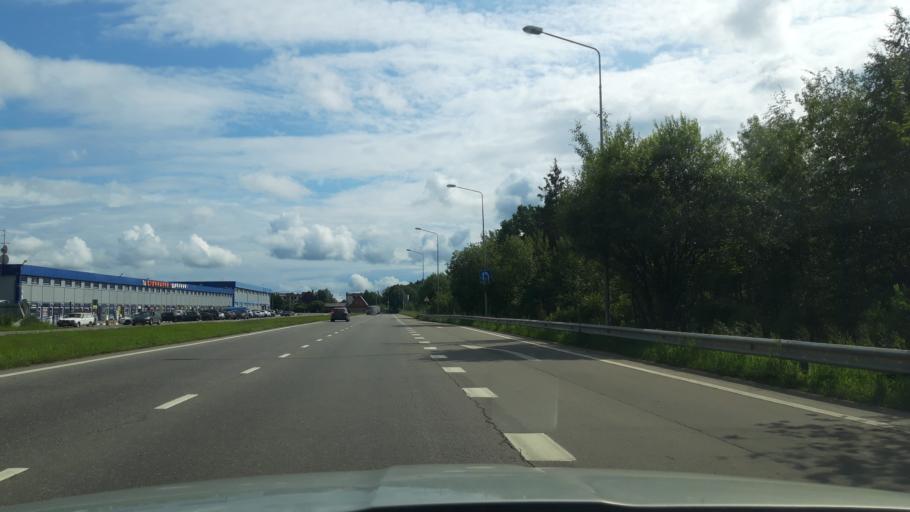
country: RU
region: Moscow
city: Zelenograd
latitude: 55.9395
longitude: 37.1752
